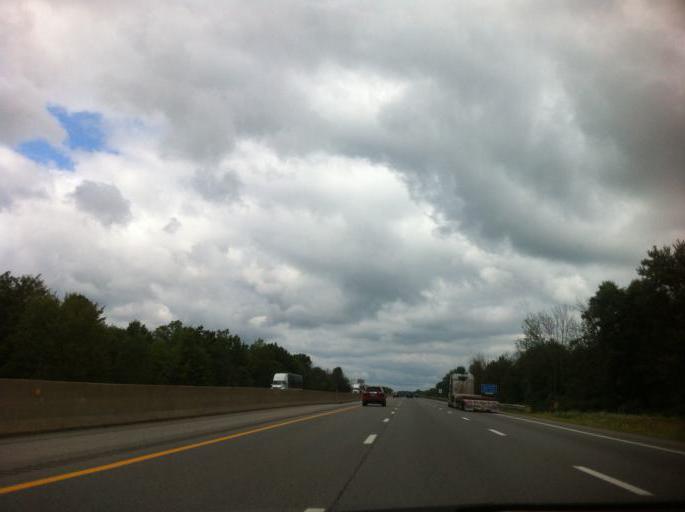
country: US
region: Ohio
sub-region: Trumbull County
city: Lordstown
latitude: 41.1624
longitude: -80.9051
